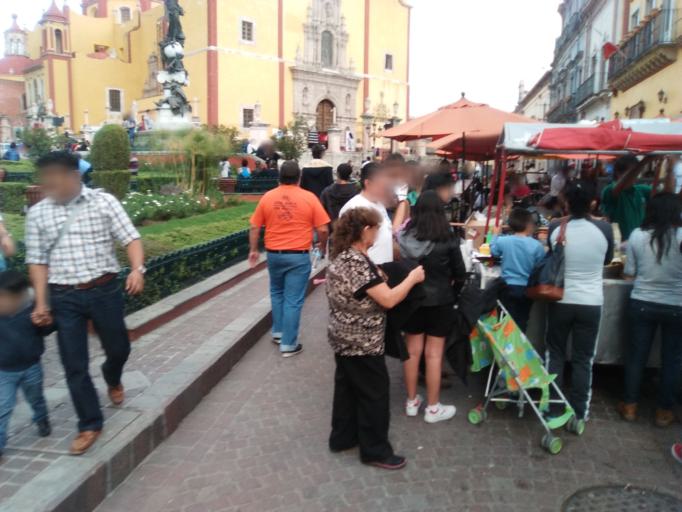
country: MX
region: Guanajuato
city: Guanajuato
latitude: 21.0168
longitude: -101.2541
